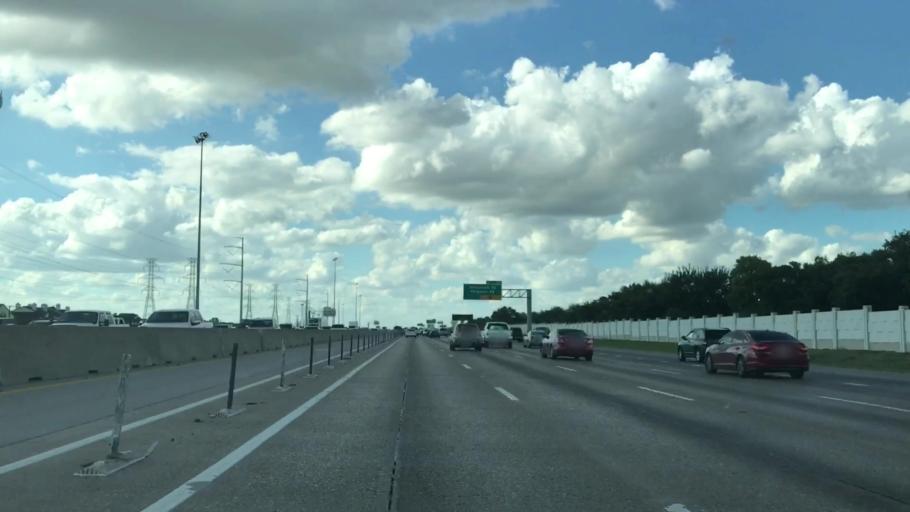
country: US
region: Texas
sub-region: Dallas County
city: Garland
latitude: 32.8481
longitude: -96.6390
